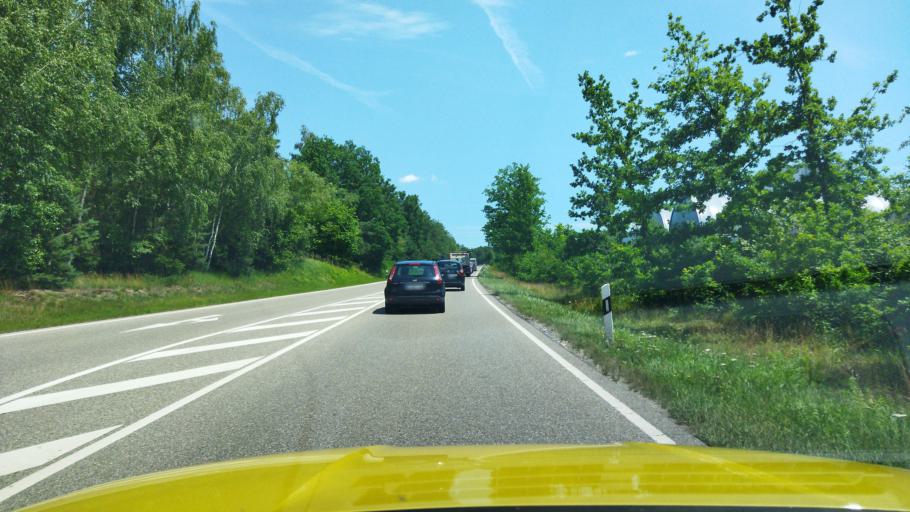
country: DE
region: Bavaria
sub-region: Regierungsbezirk Mittelfranken
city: Roth
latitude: 49.2448
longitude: 11.1369
